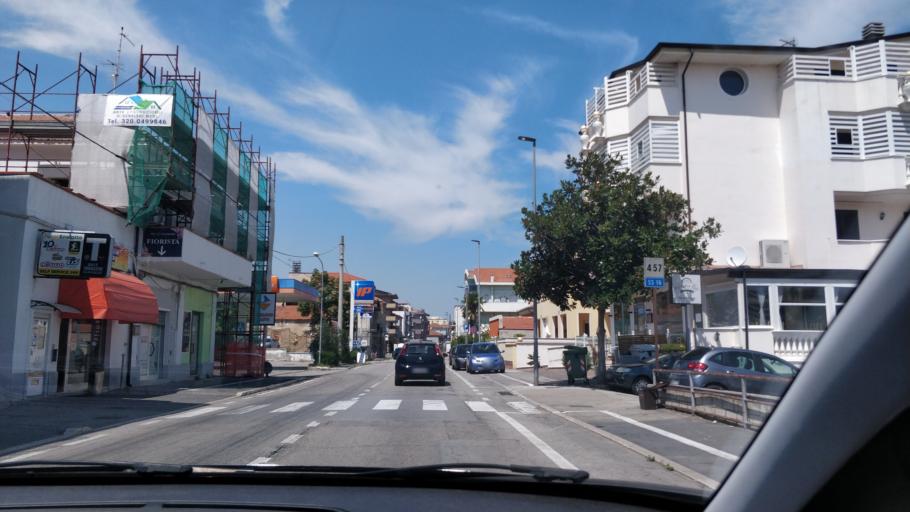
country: IT
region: Abruzzo
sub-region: Provincia di Chieti
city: Francavilla al Mare
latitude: 42.4157
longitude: 14.2974
